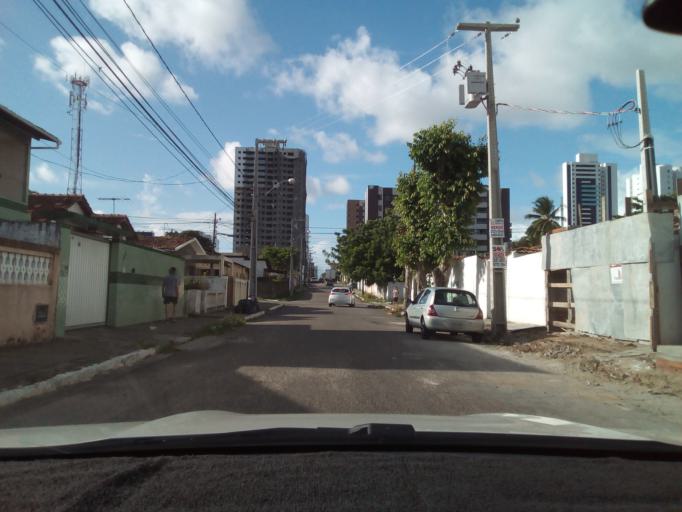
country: BR
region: Paraiba
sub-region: Joao Pessoa
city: Joao Pessoa
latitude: -7.1245
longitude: -34.8533
